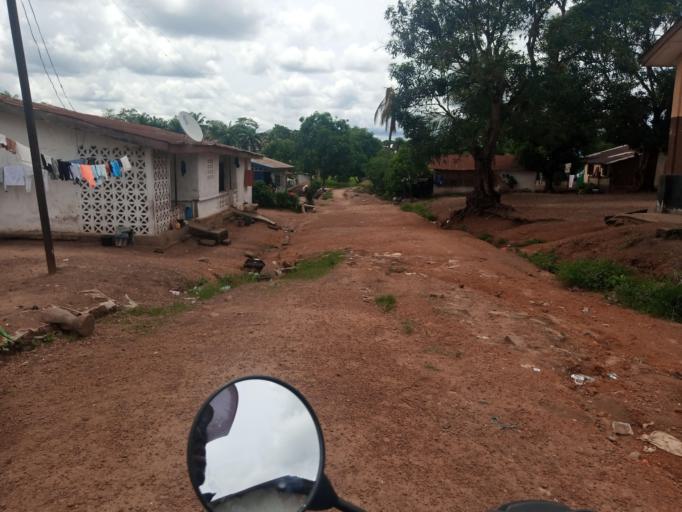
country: SL
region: Southern Province
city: Bo
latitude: 7.9558
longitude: -11.7182
